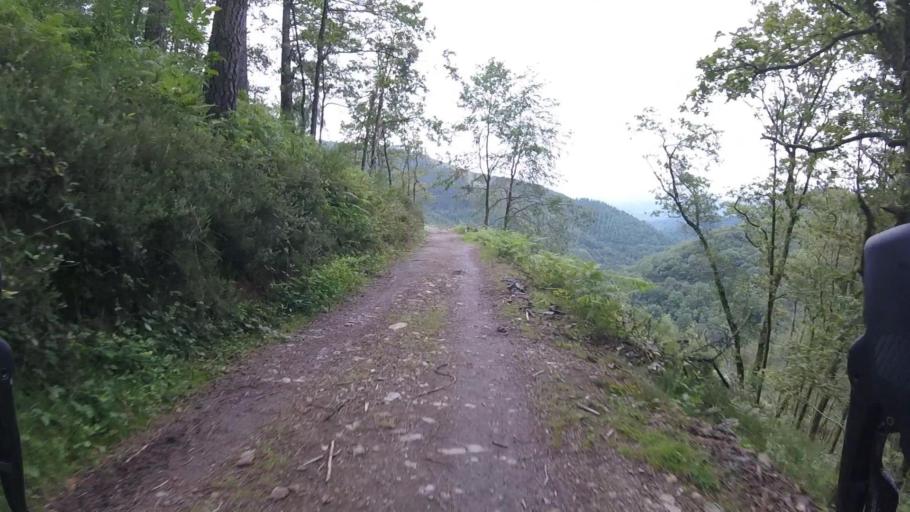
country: ES
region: Navarre
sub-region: Provincia de Navarra
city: Arano
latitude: 43.2501
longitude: -1.8655
